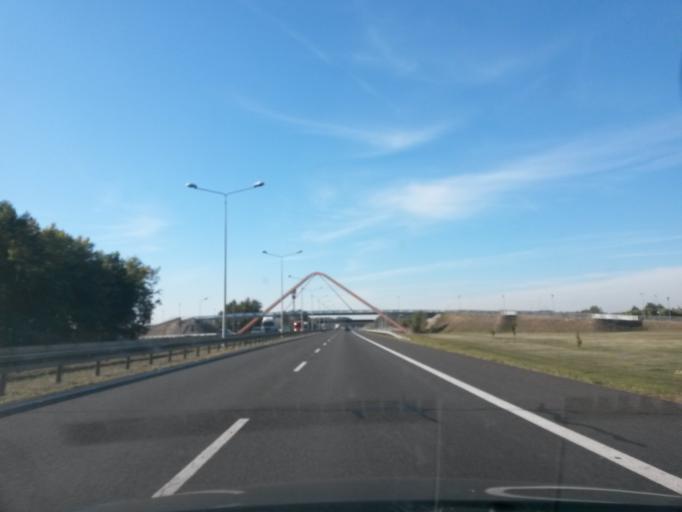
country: PL
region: Opole Voivodeship
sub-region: Powiat opolski
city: Niemodlin
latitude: 50.6763
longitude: 17.6555
